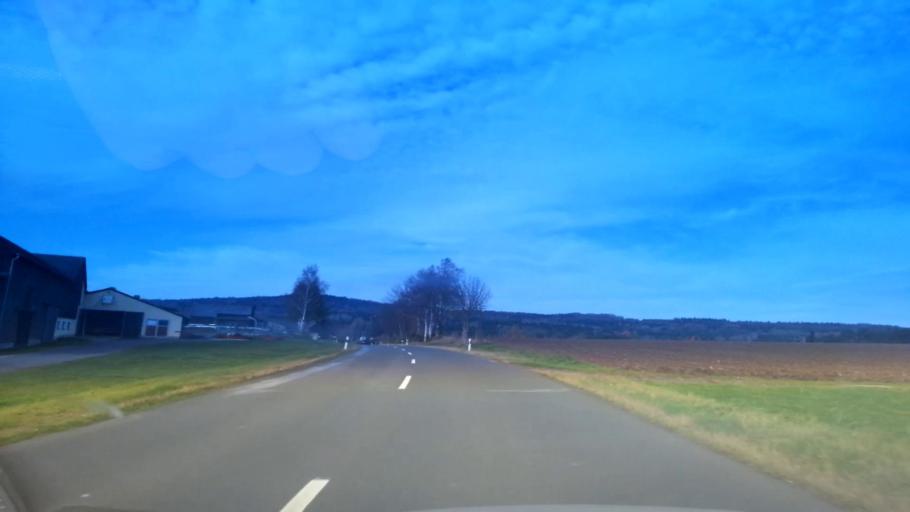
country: DE
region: Bavaria
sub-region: Upper Palatinate
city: Pechbrunn
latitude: 49.9770
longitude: 12.1773
